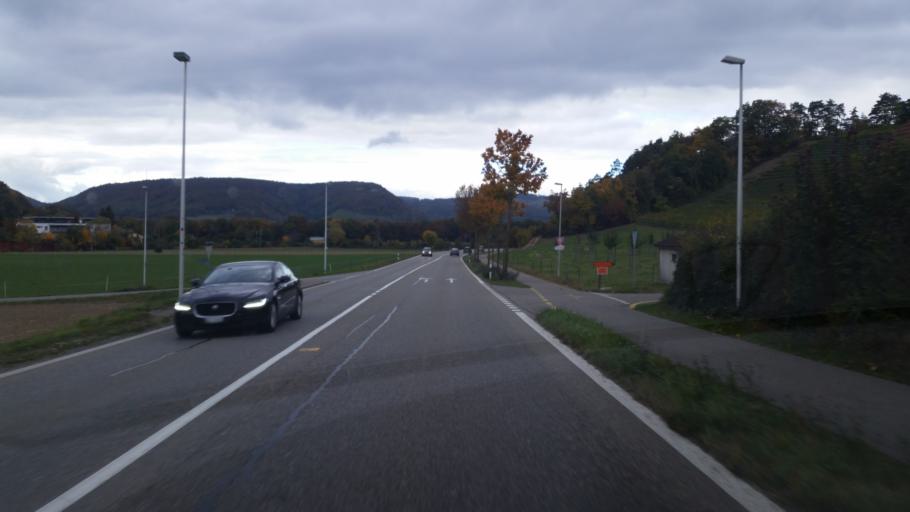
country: CH
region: Aargau
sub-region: Bezirk Brugg
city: Lauffohr (Brugg)
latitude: 47.5050
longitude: 8.2428
